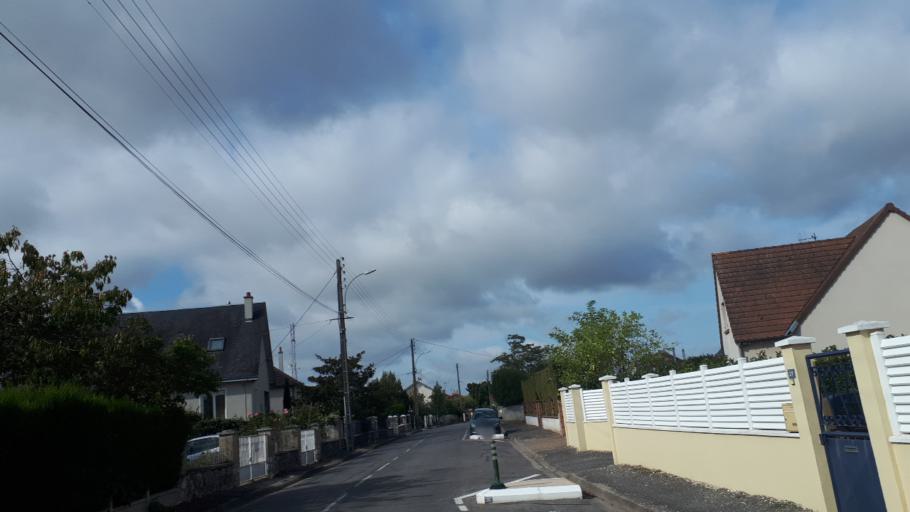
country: FR
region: Centre
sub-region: Departement du Loir-et-Cher
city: Naveil
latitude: 47.7955
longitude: 1.0405
